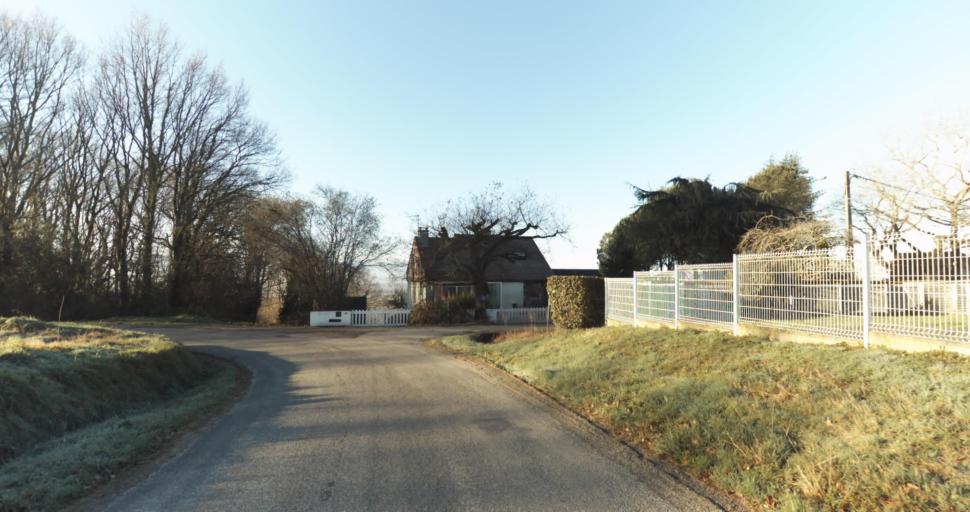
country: FR
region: Aquitaine
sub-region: Departement des Pyrenees-Atlantiques
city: Morlaas
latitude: 43.3306
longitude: -0.2677
